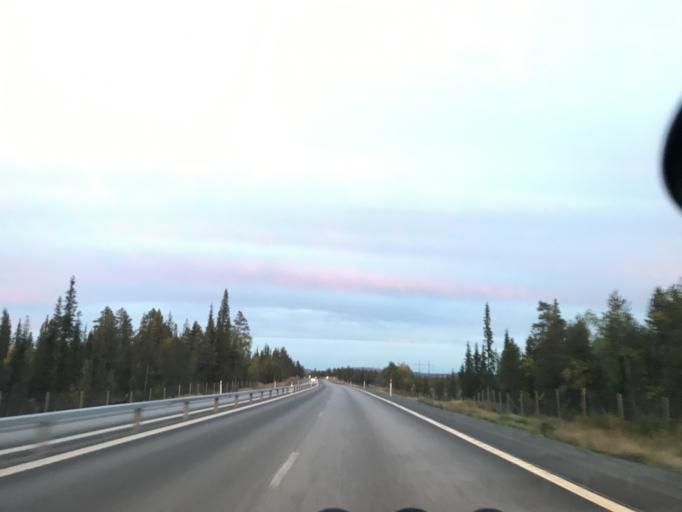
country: SE
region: Norrbotten
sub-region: Gallivare Kommun
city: Malmberget
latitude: 67.6764
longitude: 20.8932
